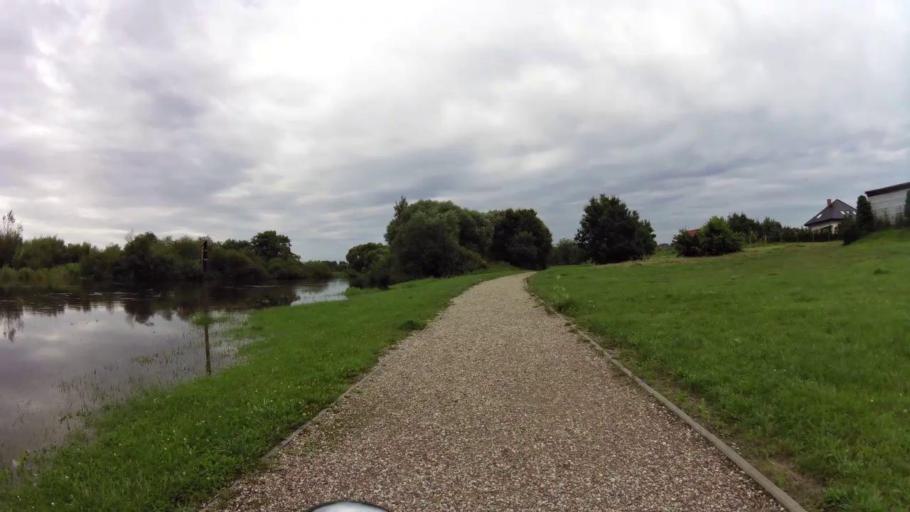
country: PL
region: West Pomeranian Voivodeship
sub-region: Powiat bialogardzki
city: Karlino
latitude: 54.0427
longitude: 15.8694
